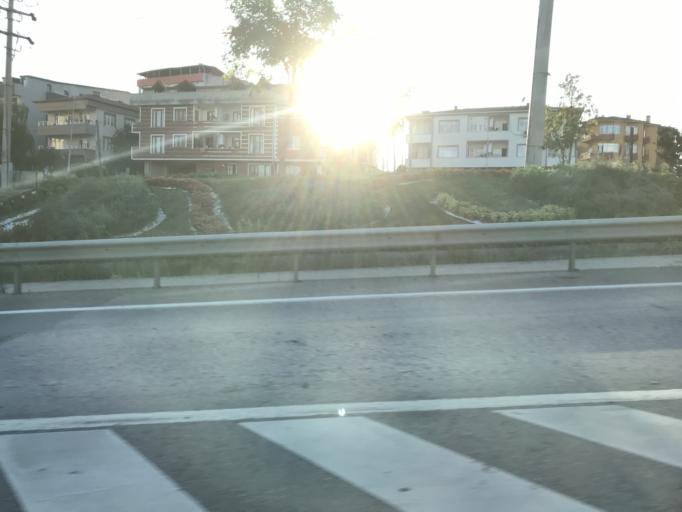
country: TR
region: Kocaeli
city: Darica
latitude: 40.7814
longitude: 29.4164
